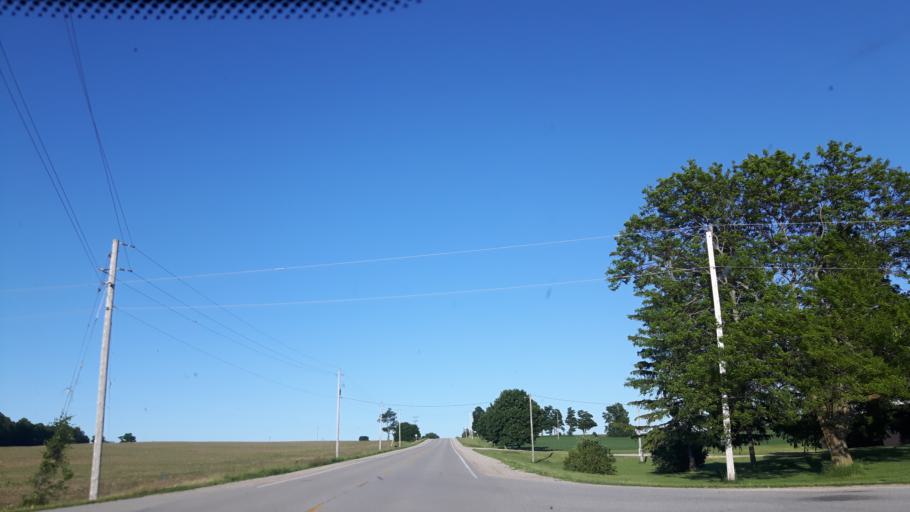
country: CA
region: Ontario
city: Goderich
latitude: 43.6427
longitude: -81.6234
